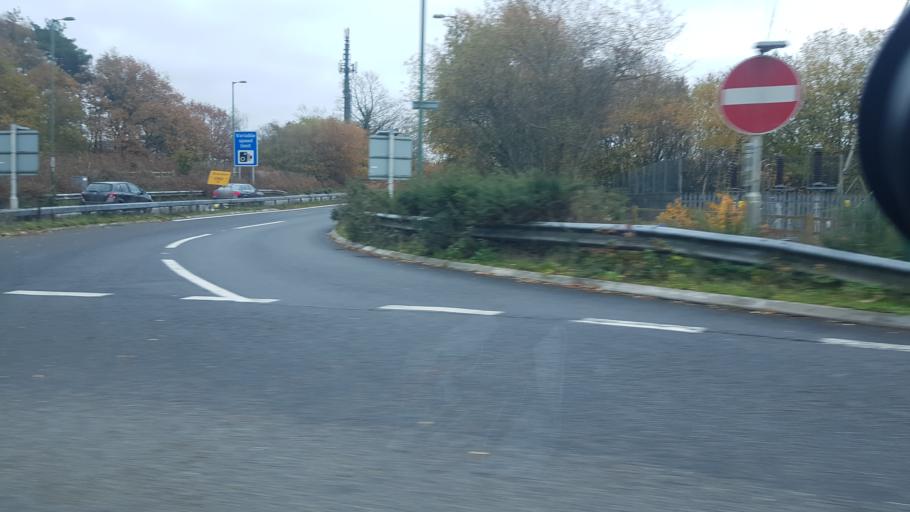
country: GB
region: England
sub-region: Hampshire
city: Fleet
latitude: 51.3045
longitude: -0.7968
